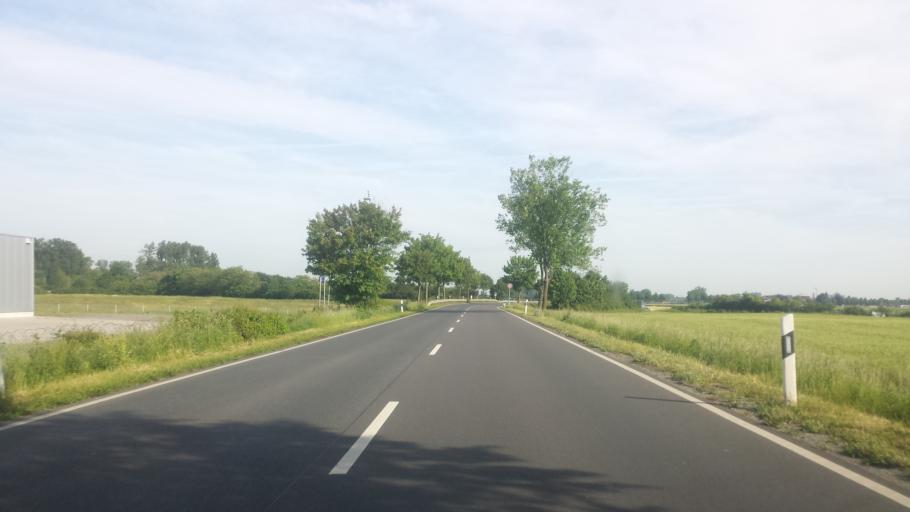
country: DE
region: Hesse
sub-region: Regierungsbezirk Darmstadt
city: Gross-Rohrheim
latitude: 49.7222
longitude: 8.4914
